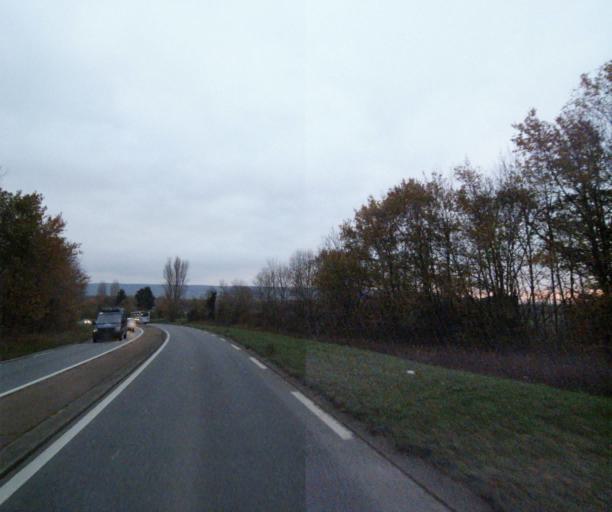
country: FR
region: Ile-de-France
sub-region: Departement des Yvelines
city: Medan
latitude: 48.9542
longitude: 1.9802
